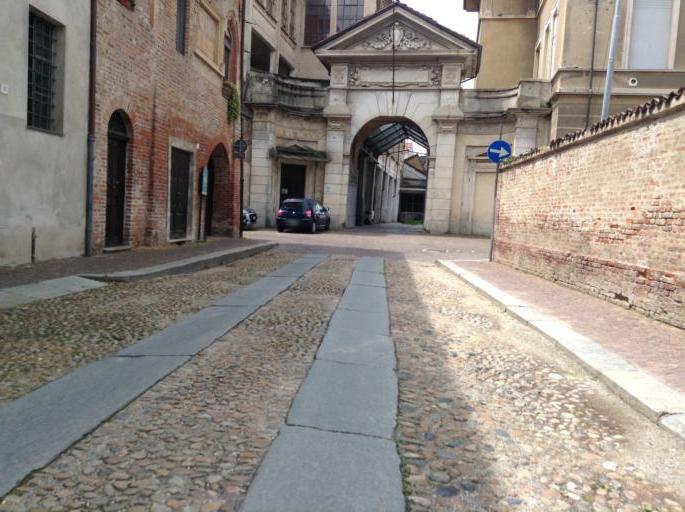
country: IT
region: Piedmont
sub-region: Provincia di Torino
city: Carignano
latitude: 44.9075
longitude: 7.6763
